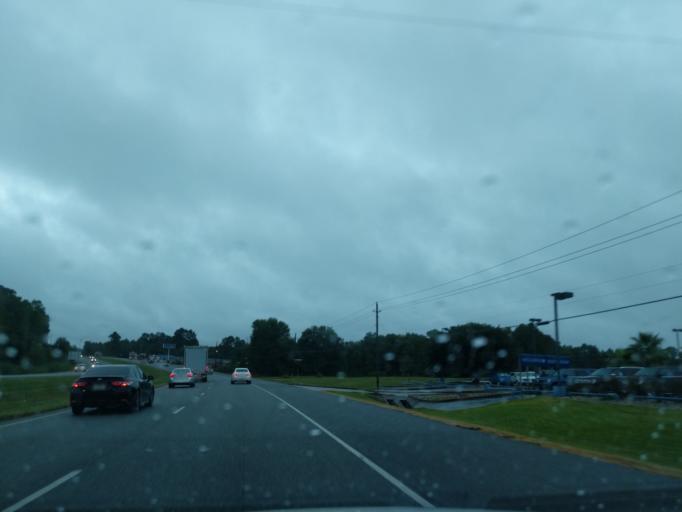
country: US
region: Texas
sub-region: Angelina County
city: Lufkin
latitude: 31.3433
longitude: -94.6915
